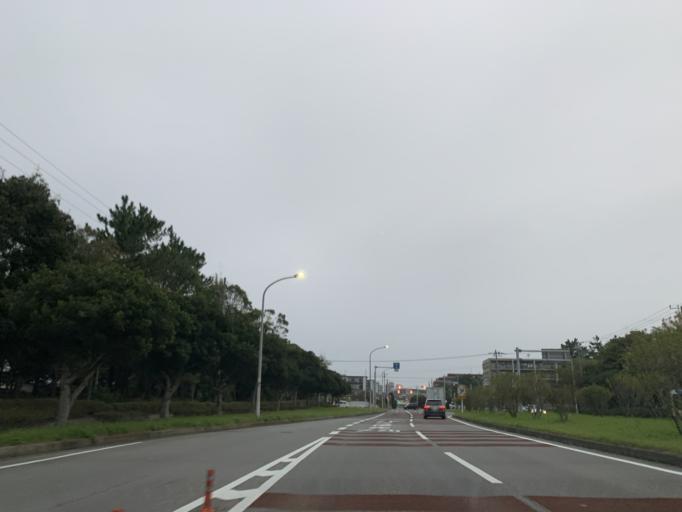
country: JP
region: Chiba
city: Funabashi
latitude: 35.6623
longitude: 140.0352
